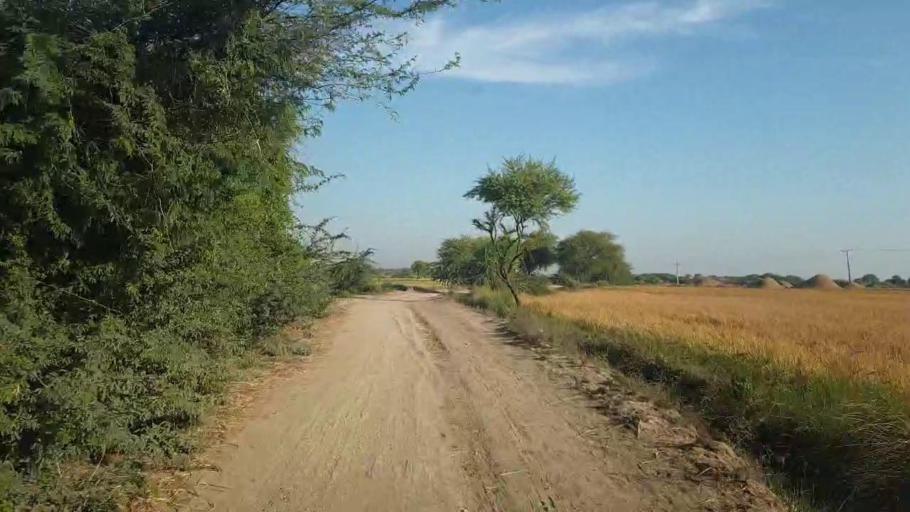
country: PK
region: Sindh
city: Talhar
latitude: 24.8100
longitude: 68.8388
